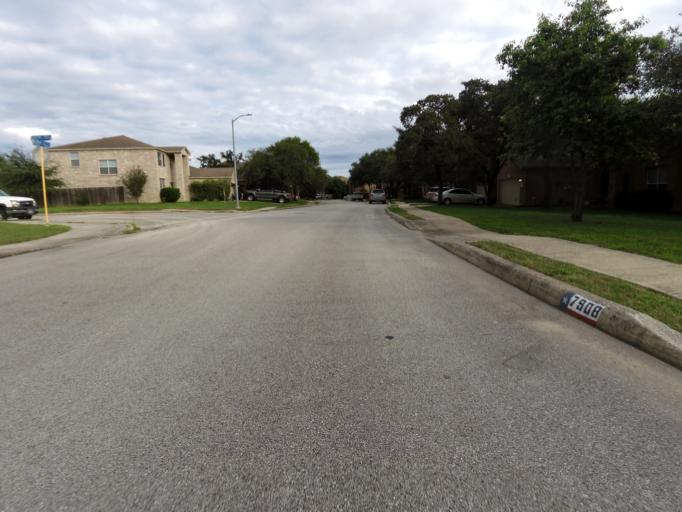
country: US
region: Texas
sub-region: Bexar County
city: Cross Mountain
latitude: 29.6686
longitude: -98.6383
